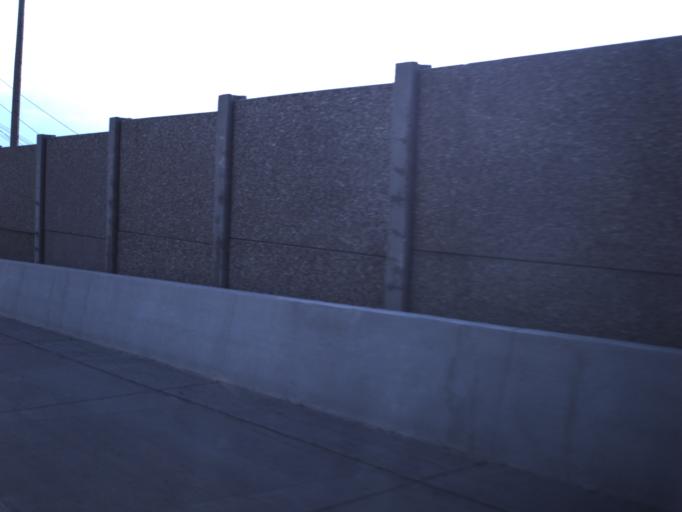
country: US
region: Utah
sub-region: Salt Lake County
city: Holladay
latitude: 40.6599
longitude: -111.8065
